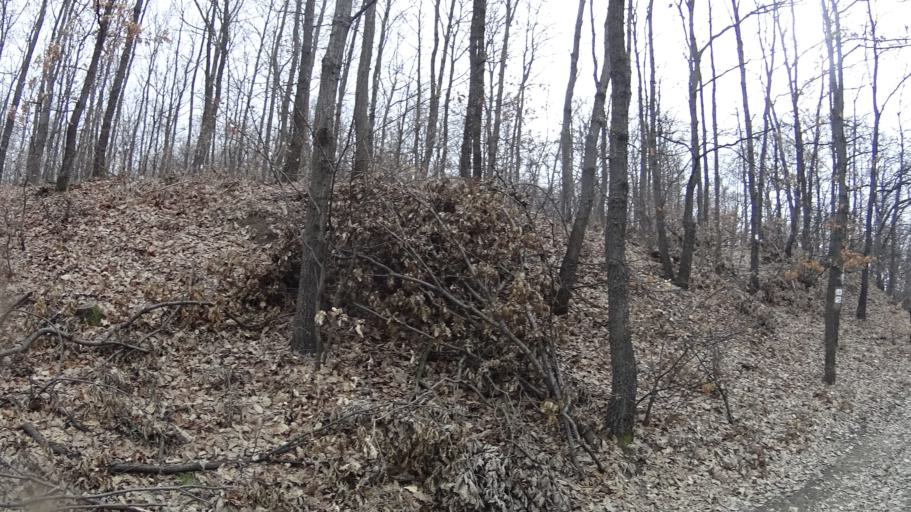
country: HU
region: Pest
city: Kosd
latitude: 47.8276
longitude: 19.1757
